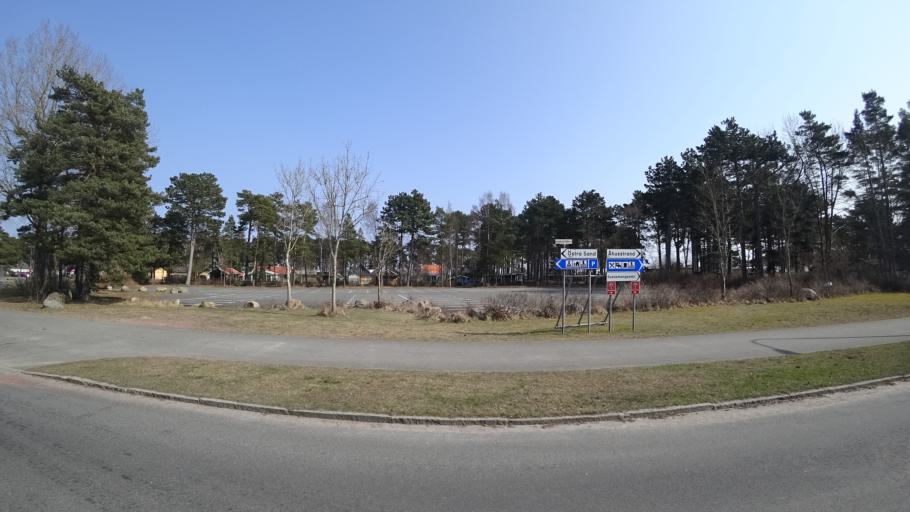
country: SE
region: Skane
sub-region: Kristianstads Kommun
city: Ahus
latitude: 55.9386
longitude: 14.3160
